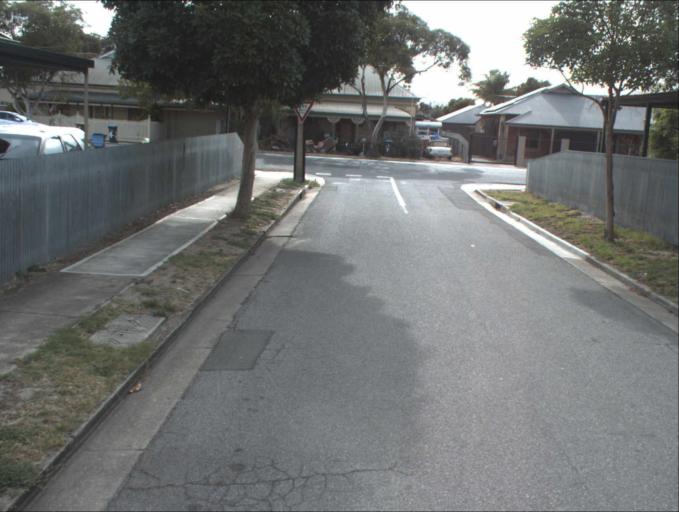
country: AU
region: South Australia
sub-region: Port Adelaide Enfield
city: Birkenhead
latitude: -34.8292
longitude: 138.4956
